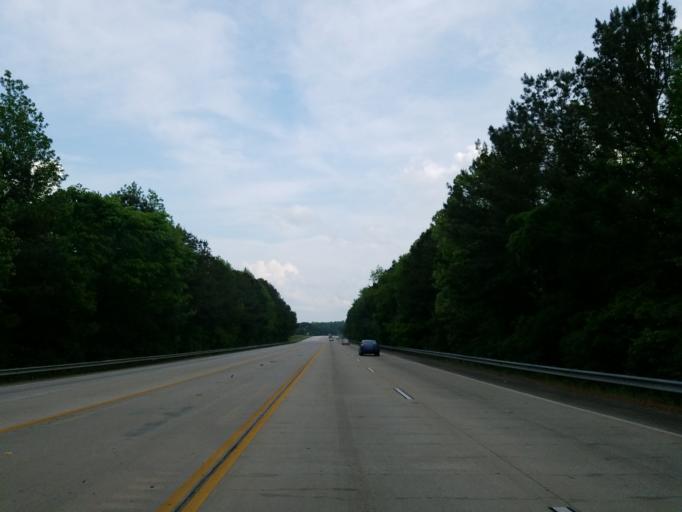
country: US
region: Georgia
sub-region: Douglas County
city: Lithia Springs
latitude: 33.8248
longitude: -84.6634
